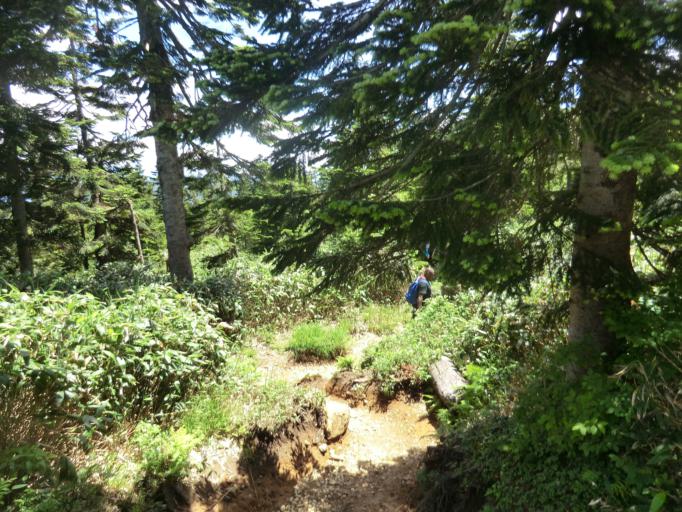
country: JP
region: Gunma
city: Numata
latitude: 36.8893
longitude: 139.1736
